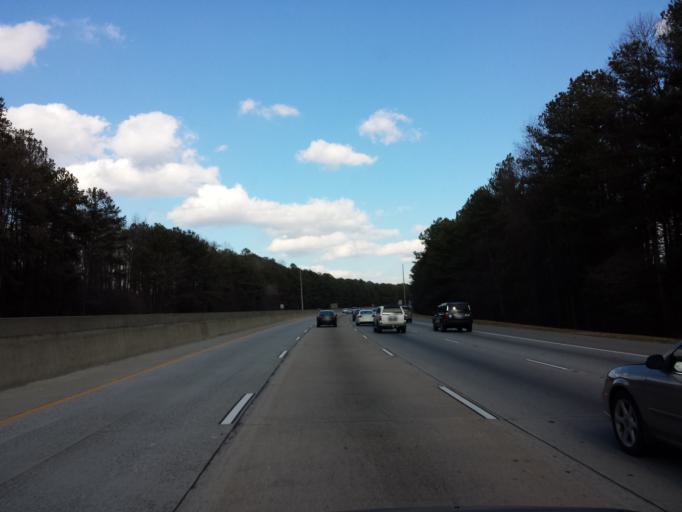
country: US
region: Georgia
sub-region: Fulton County
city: Alpharetta
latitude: 34.0473
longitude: -84.3030
